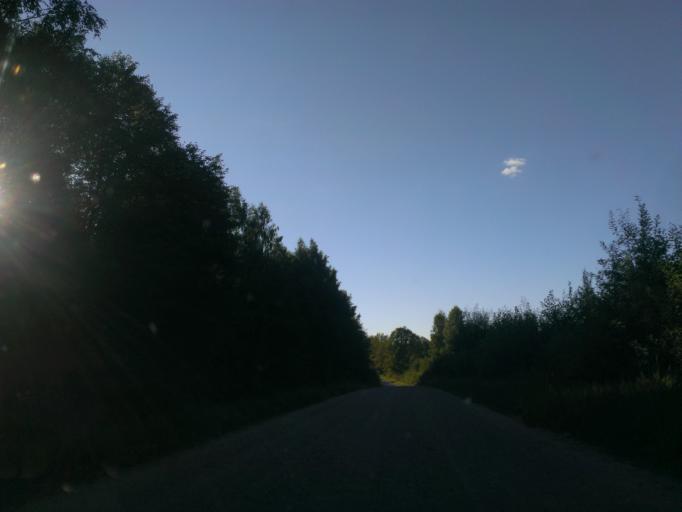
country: LV
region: Malpils
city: Malpils
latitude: 57.0842
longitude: 25.0567
